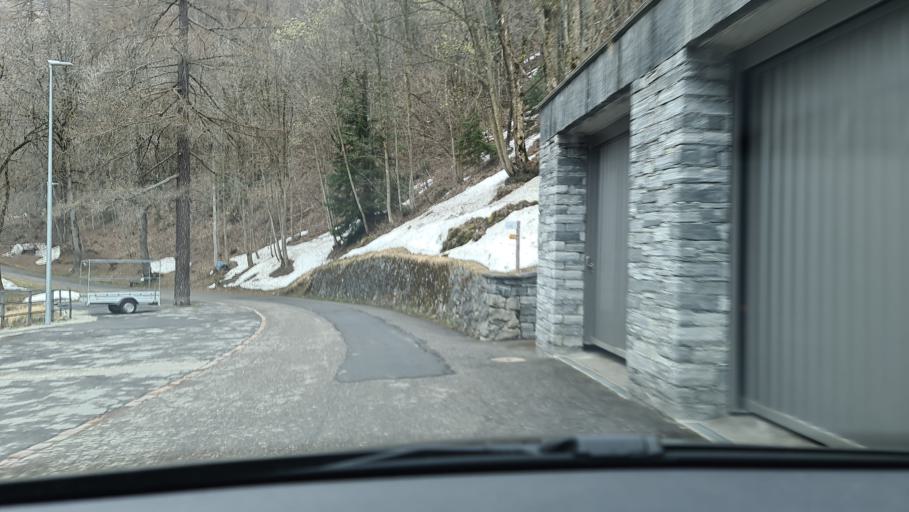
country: CH
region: Ticino
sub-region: Leventina District
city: Airolo
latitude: 46.4437
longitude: 8.6644
